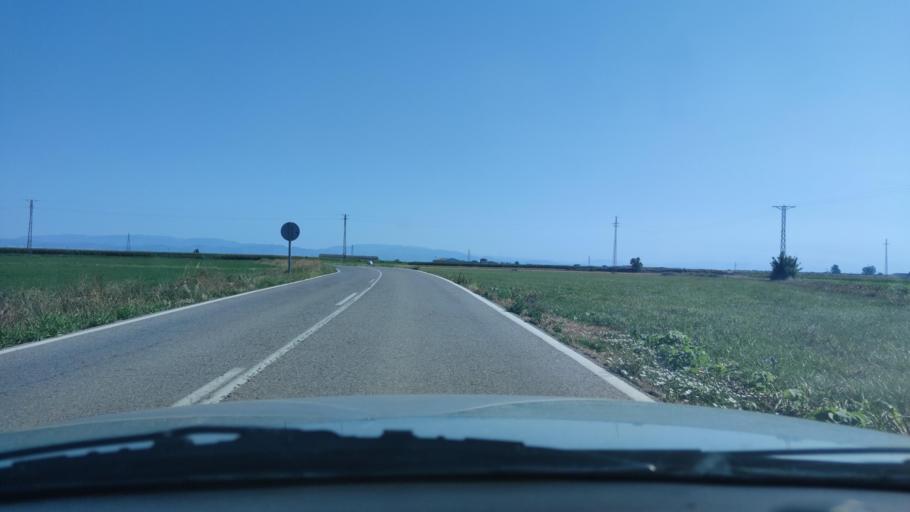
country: ES
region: Catalonia
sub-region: Provincia de Lleida
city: Bellvis
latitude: 41.6411
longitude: 0.7944
